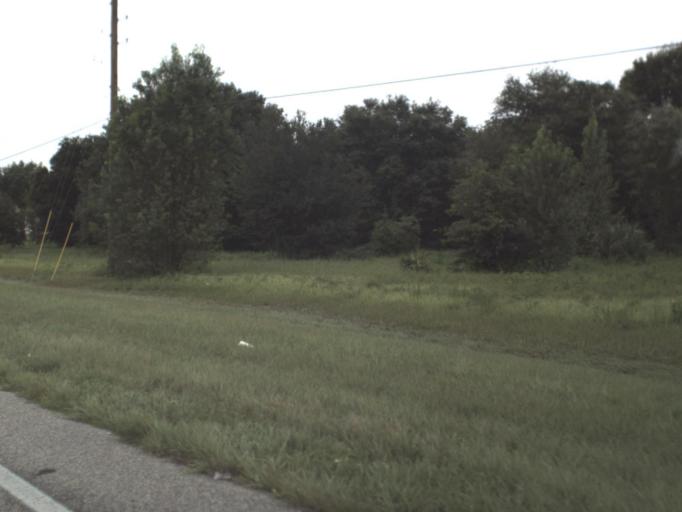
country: US
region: Florida
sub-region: Polk County
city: Eagle Lake
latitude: 27.9480
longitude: -81.7929
